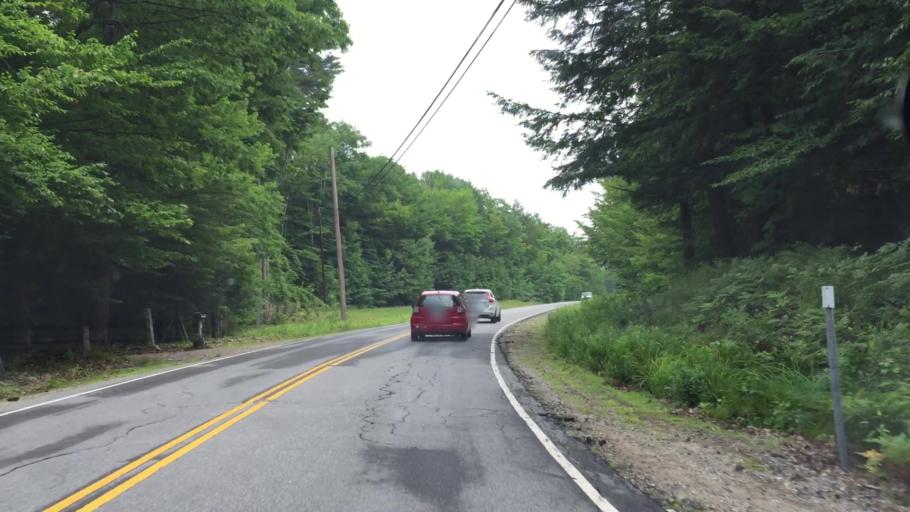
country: US
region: New Hampshire
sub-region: Carroll County
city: Sandwich
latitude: 43.7877
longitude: -71.4635
